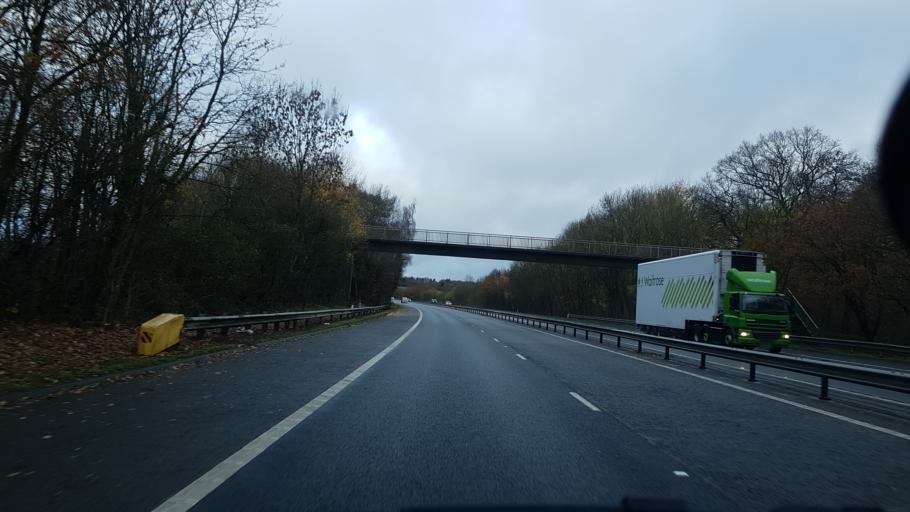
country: GB
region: England
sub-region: Wokingham
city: Wokingham
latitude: 51.4215
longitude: -0.8138
